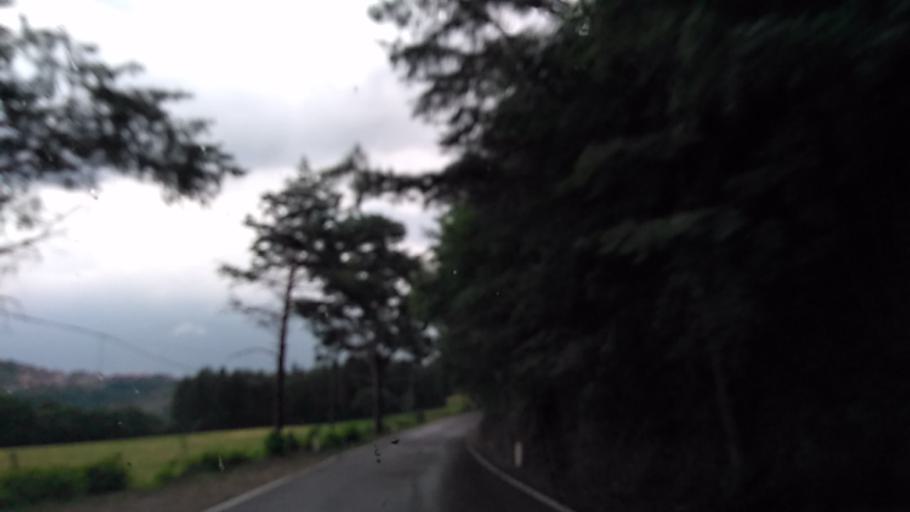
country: IT
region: Lombardy
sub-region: Provincia di Brescia
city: Gardola
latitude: 45.7588
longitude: 10.7226
